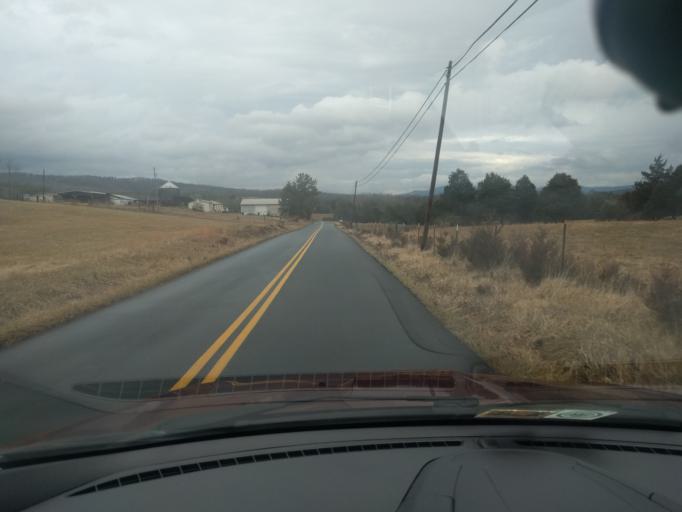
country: US
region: Virginia
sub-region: Botetourt County
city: Fincastle
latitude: 37.5345
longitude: -79.8802
